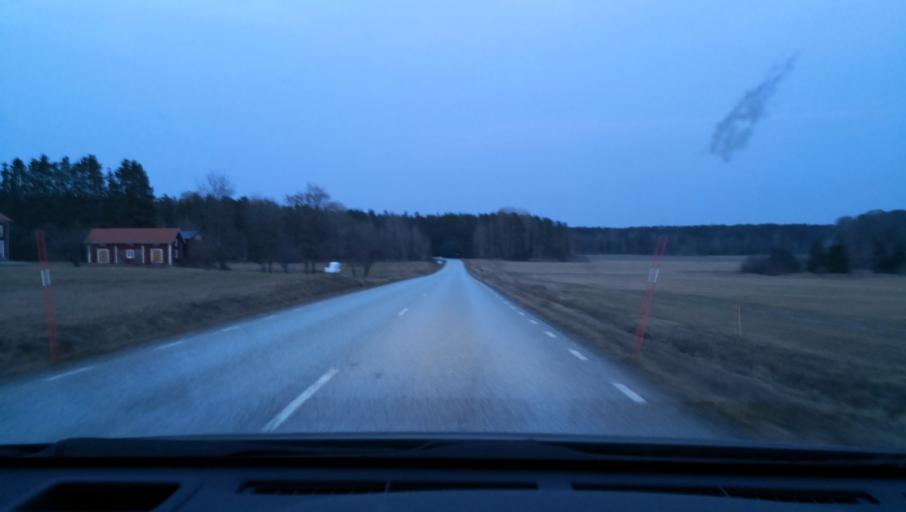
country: SE
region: OErebro
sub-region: Lindesbergs Kommun
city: Lindesberg
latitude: 59.5939
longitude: 15.3014
